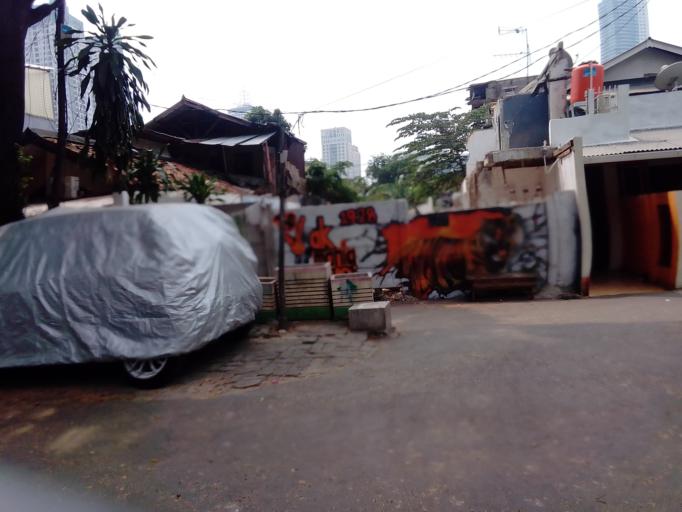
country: ID
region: Jakarta Raya
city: Jakarta
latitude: -6.2006
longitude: 106.8187
